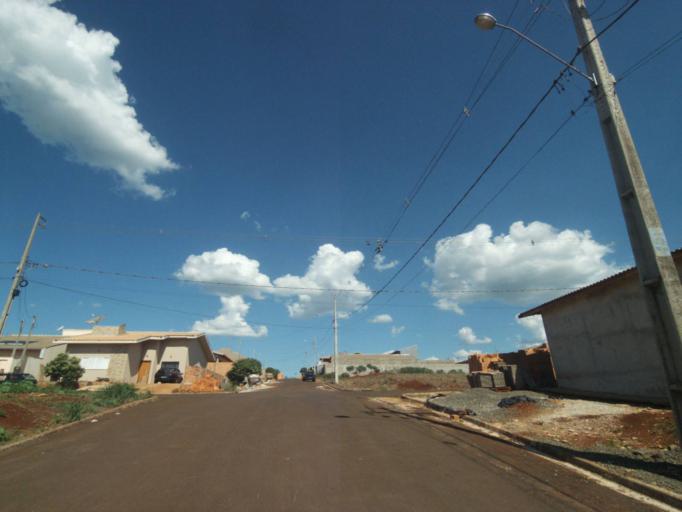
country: BR
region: Parana
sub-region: Sertanopolis
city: Sertanopolis
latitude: -23.0375
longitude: -50.8117
